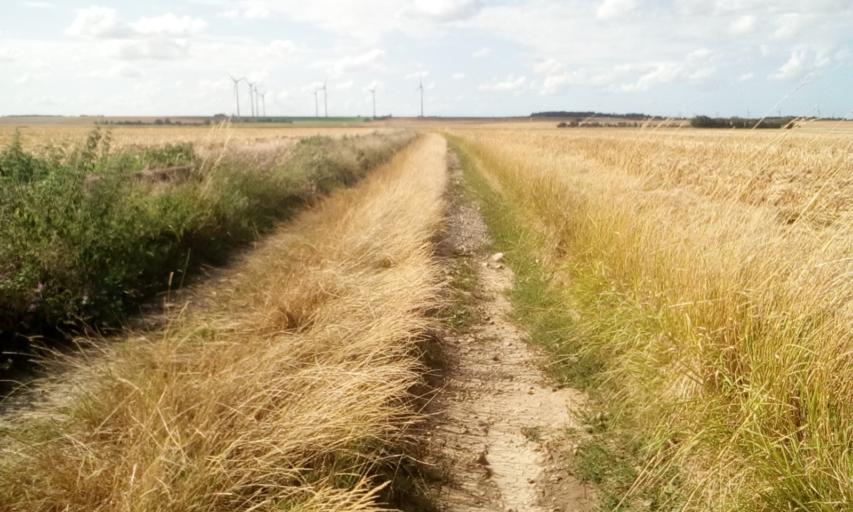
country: FR
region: Lower Normandy
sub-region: Departement du Calvados
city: Saint-Sylvain
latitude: 49.0787
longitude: -0.2366
